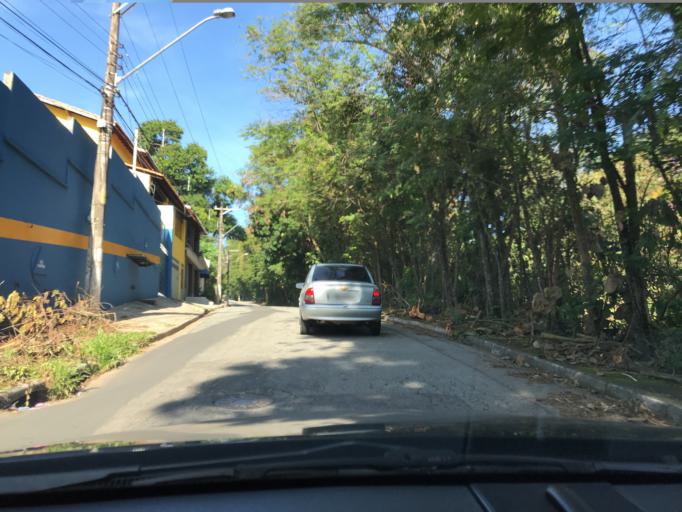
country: BR
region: Sao Paulo
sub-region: Itapevi
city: Itapevi
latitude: -23.5354
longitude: -46.9417
